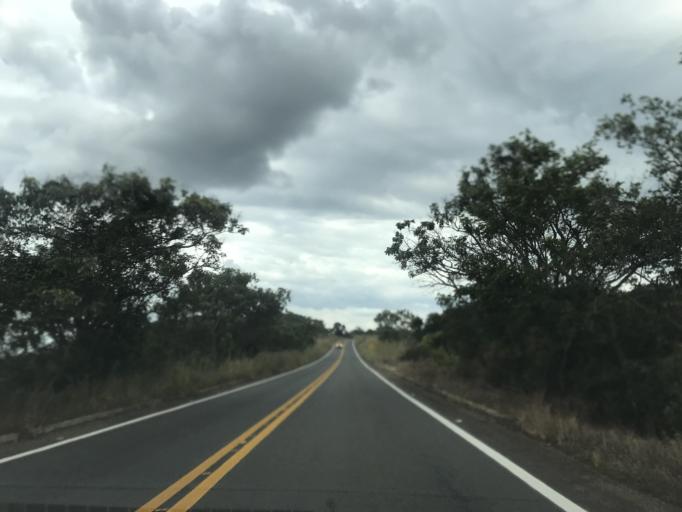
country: BR
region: Goias
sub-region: Bela Vista De Goias
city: Bela Vista de Goias
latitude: -17.0160
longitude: -48.6590
